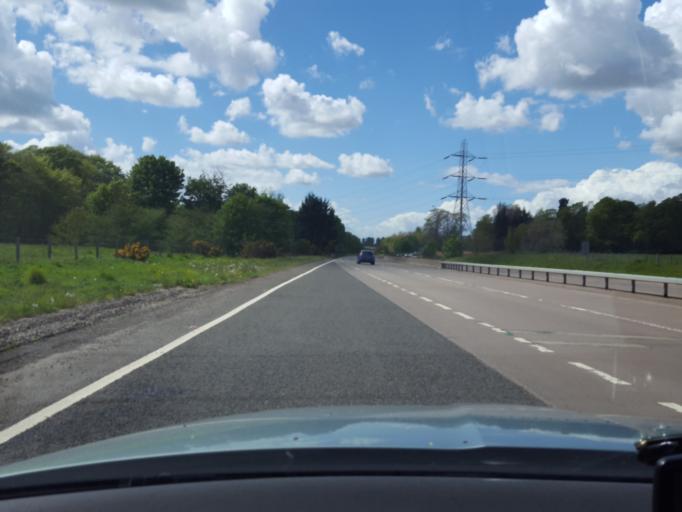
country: GB
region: Scotland
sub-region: Angus
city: Brechin
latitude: 56.7280
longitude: -2.7030
